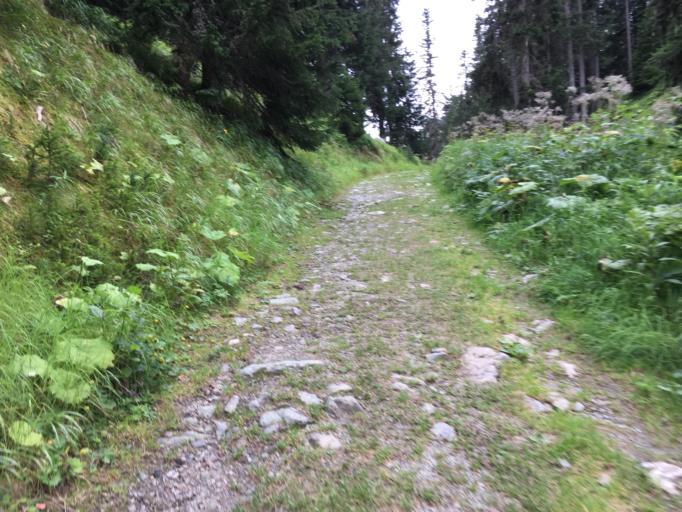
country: CH
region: Grisons
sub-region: Maloja District
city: Silvaplana
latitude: 46.4864
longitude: 9.6501
